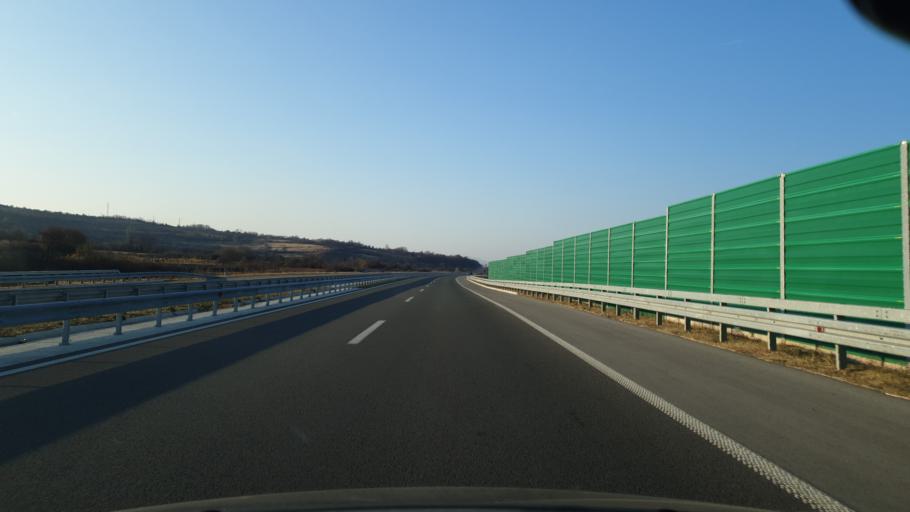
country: RS
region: Central Serbia
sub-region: Pirotski Okrug
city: Dimitrovgrad
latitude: 43.0478
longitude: 22.7037
